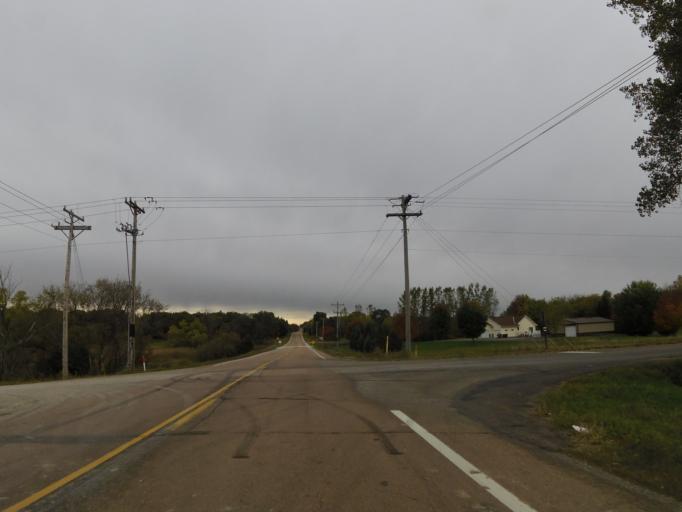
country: US
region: Minnesota
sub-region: Scott County
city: Prior Lake
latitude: 44.6887
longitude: -93.4604
